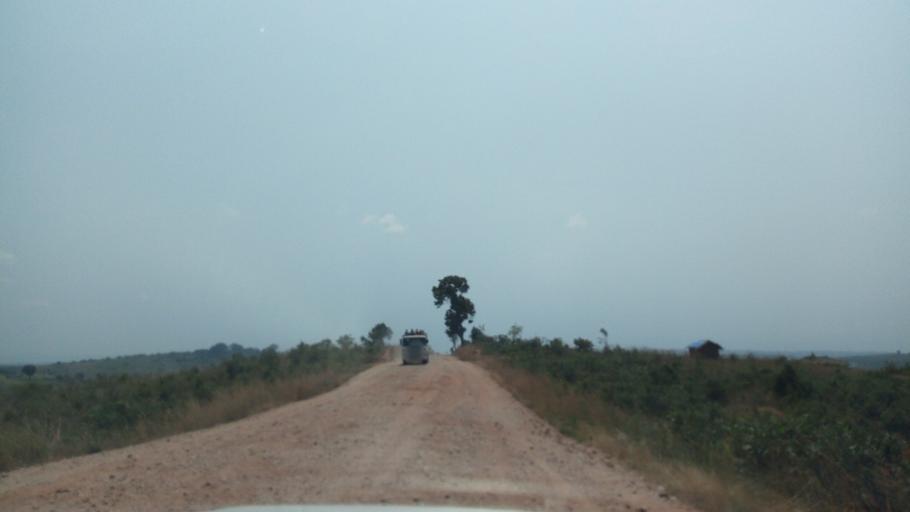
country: CD
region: Katanga
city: Kalemie
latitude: -5.8694
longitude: 29.1738
